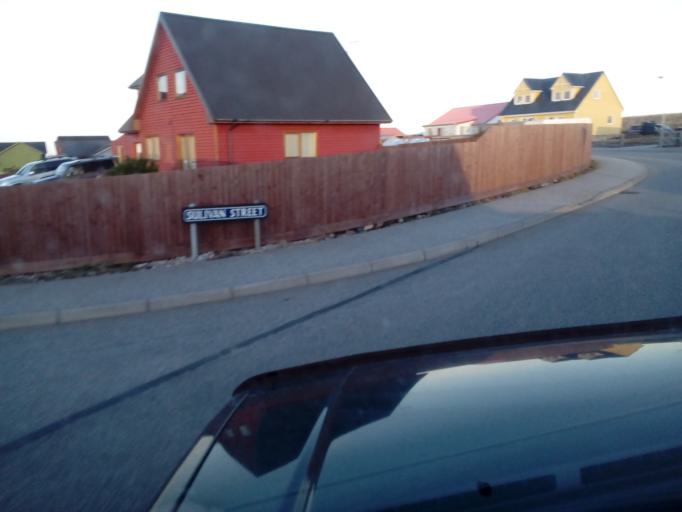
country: FK
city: Stanley
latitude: -51.6965
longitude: -57.8351
